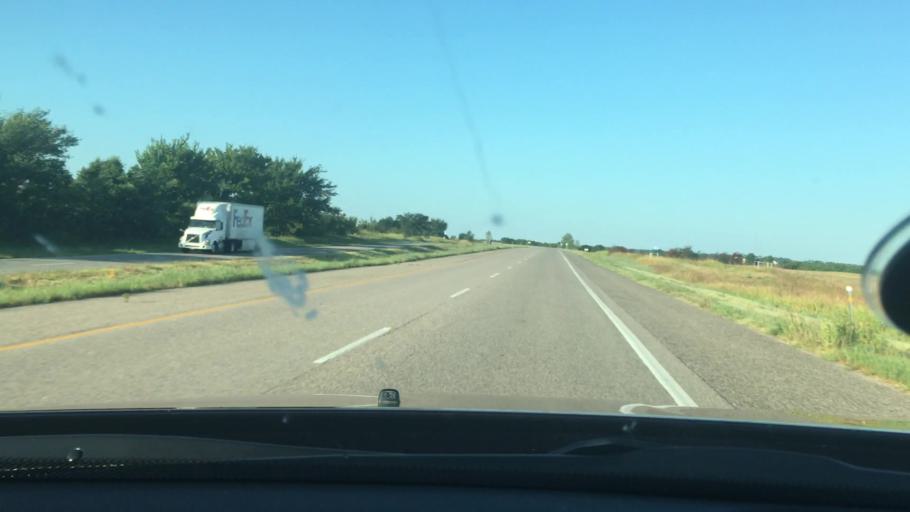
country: US
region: Oklahoma
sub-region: Pontotoc County
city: Ada
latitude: 34.7135
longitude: -96.7269
